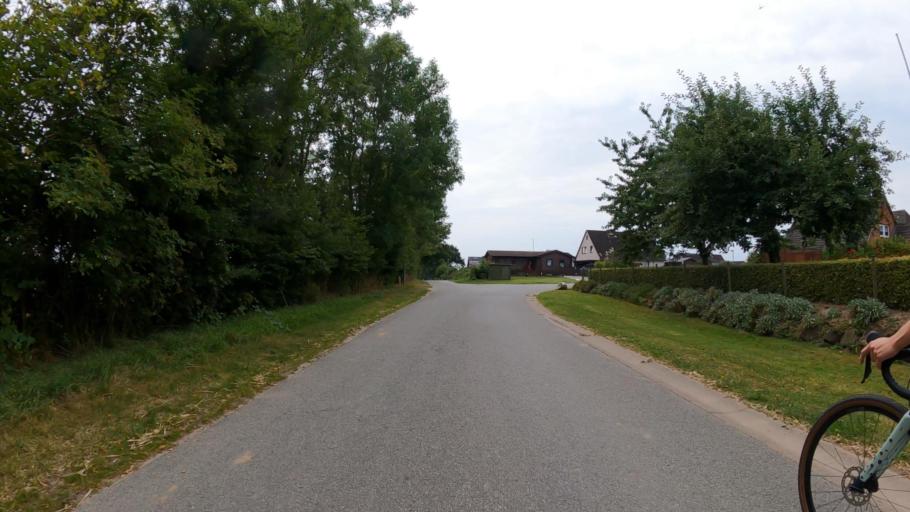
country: DE
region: Schleswig-Holstein
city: Fredesdorf
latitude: 53.8645
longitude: 10.2208
